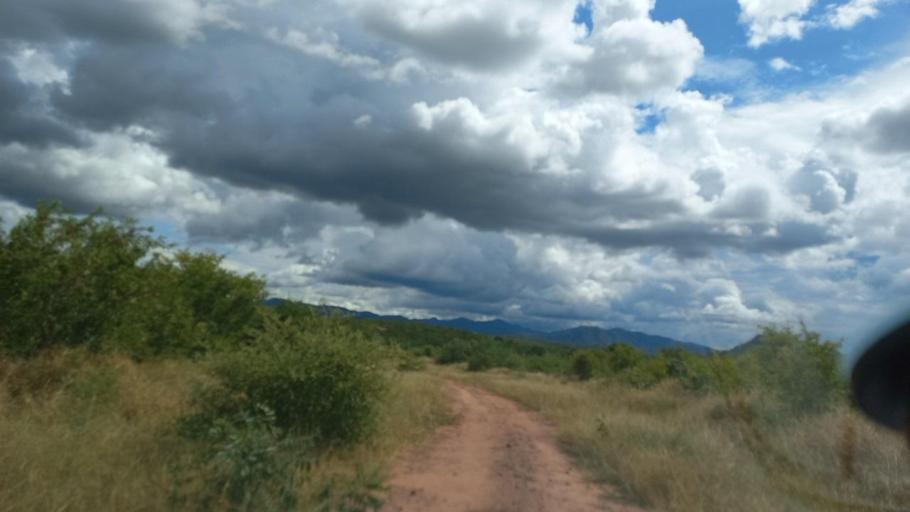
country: ZM
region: Lusaka
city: Luangwa
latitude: -15.6290
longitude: 30.3891
